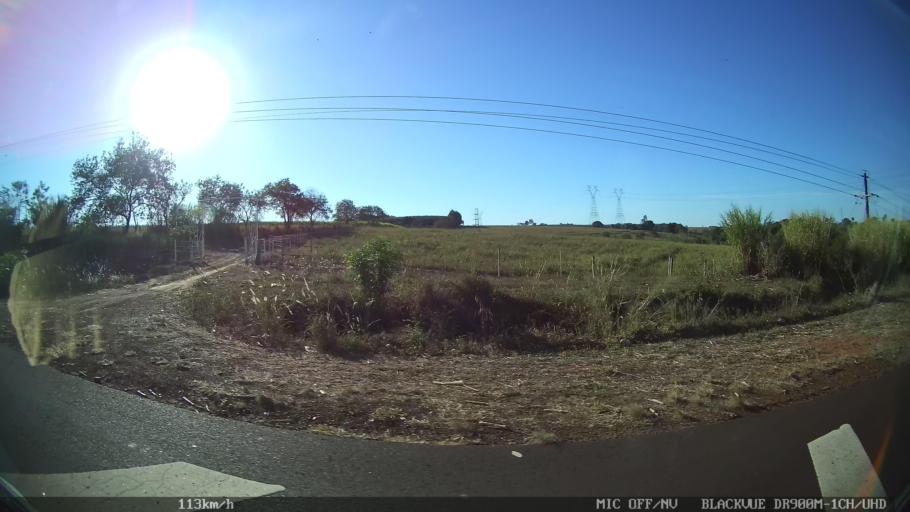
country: BR
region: Sao Paulo
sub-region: Olimpia
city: Olimpia
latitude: -20.7082
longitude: -48.9662
